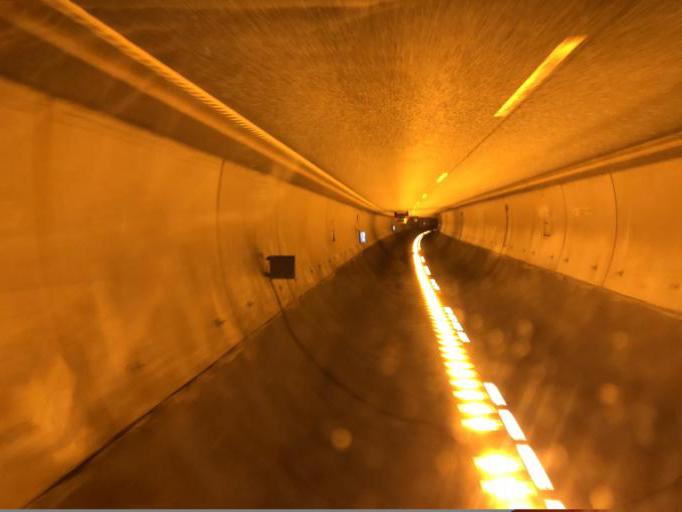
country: NO
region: Vestfold
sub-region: Holmestrand
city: Holmestrand
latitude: 59.4589
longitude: 10.3438
